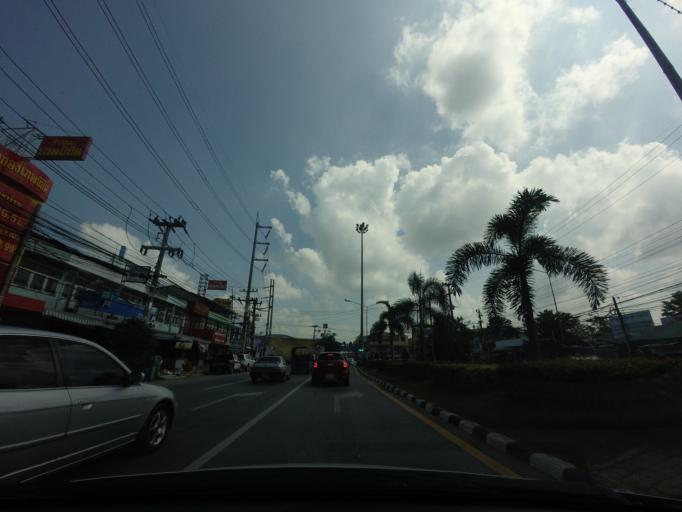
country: TH
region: Nakhon Pathom
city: Nakhon Chai Si
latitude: 13.8015
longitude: 100.1839
